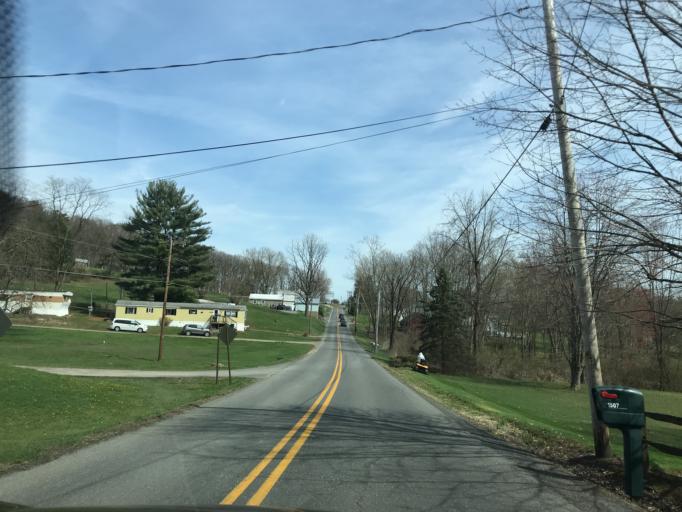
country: US
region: Pennsylvania
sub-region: Northumberland County
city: Northumberland
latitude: 40.8871
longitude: -76.8241
